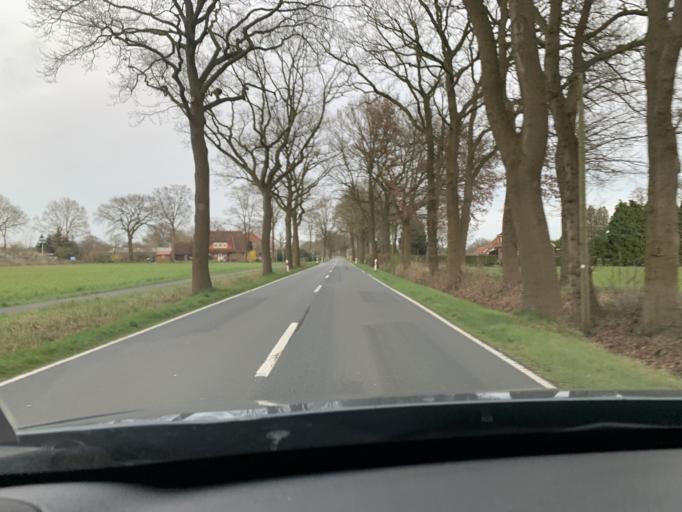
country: DE
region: Lower Saxony
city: Apen
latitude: 53.1774
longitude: 7.8031
